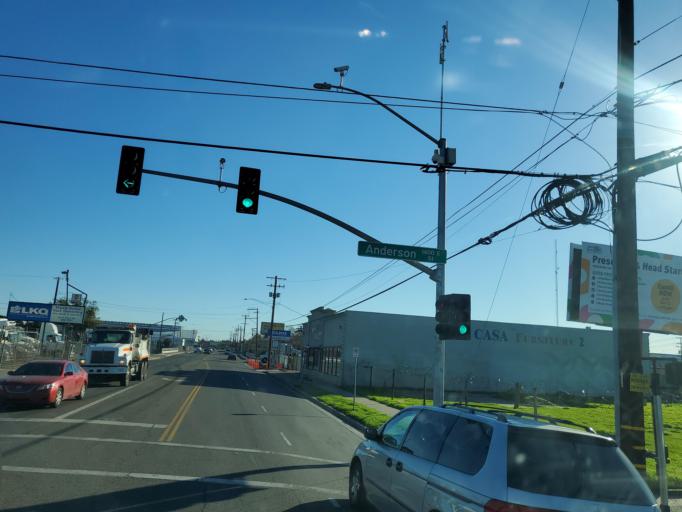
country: US
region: California
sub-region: San Joaquin County
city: Kennedy
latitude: 37.9459
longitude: -121.2689
